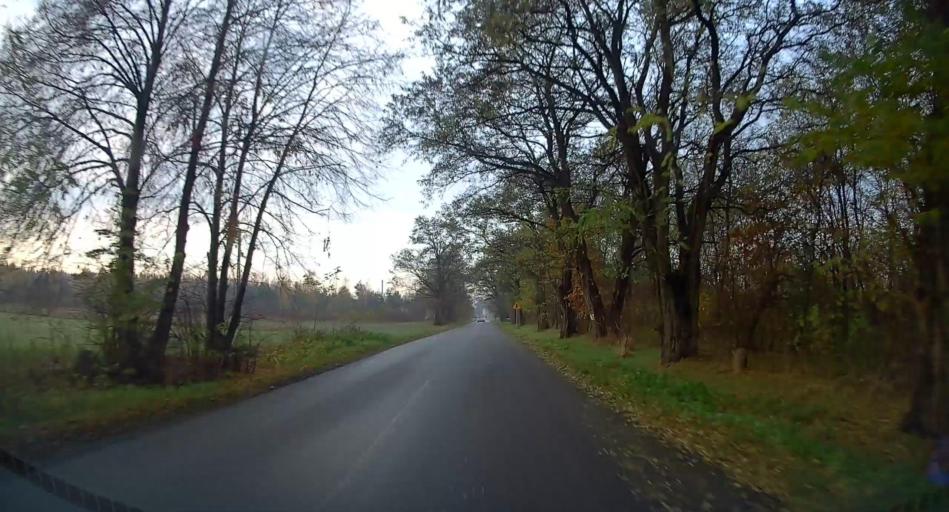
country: PL
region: Masovian Voivodeship
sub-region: Powiat zyrardowski
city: Puszcza Marianska
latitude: 51.9310
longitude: 20.3619
